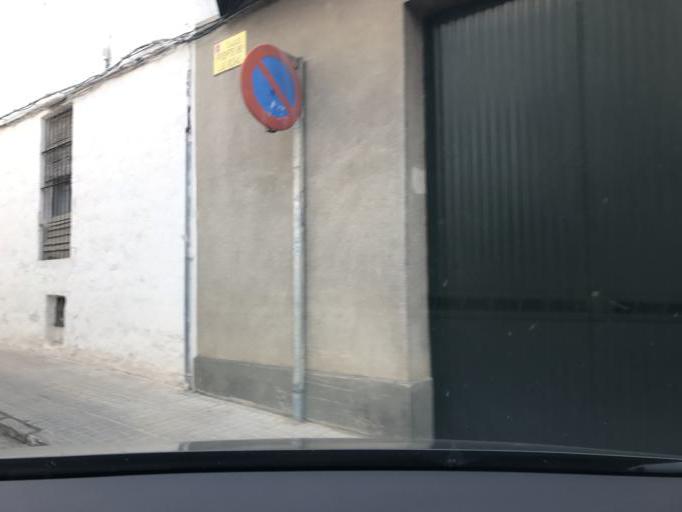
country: ES
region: Andalusia
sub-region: Provincia de Jaen
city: Ubeda
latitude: 38.0091
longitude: -3.3752
